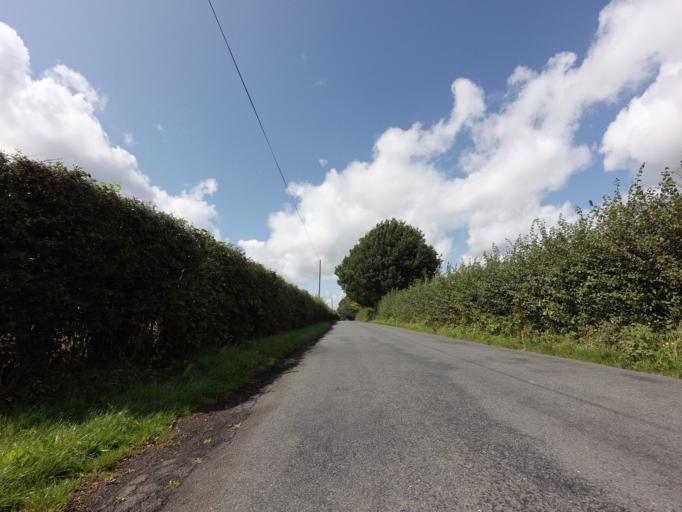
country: GB
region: England
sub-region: Kent
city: Hadlow
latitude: 51.2365
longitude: 0.3292
